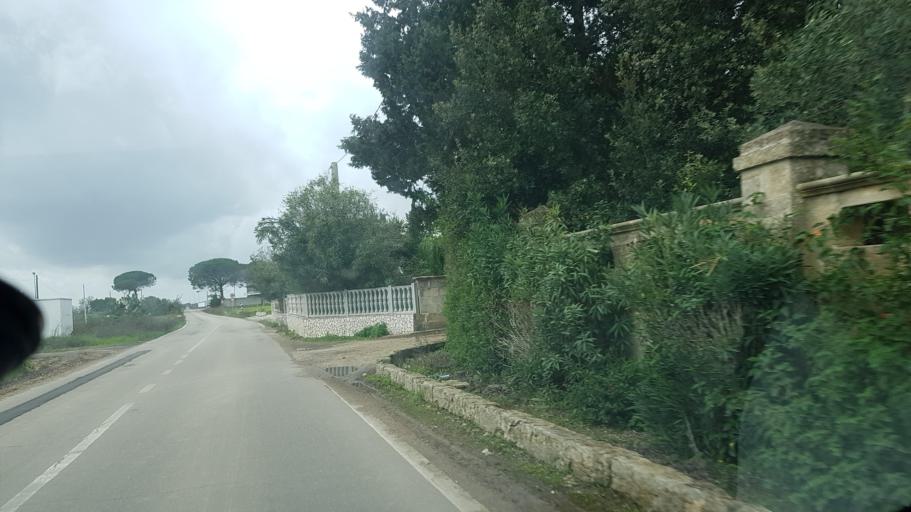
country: IT
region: Apulia
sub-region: Provincia di Lecce
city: Novoli
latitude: 40.3700
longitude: 18.0457
